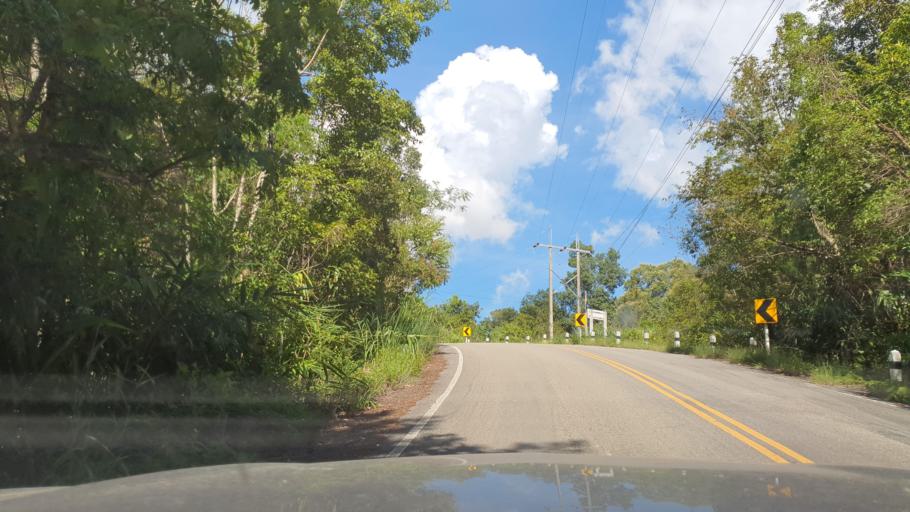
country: TH
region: Chiang Rai
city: Wiang Pa Pao
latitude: 19.3046
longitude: 99.3721
